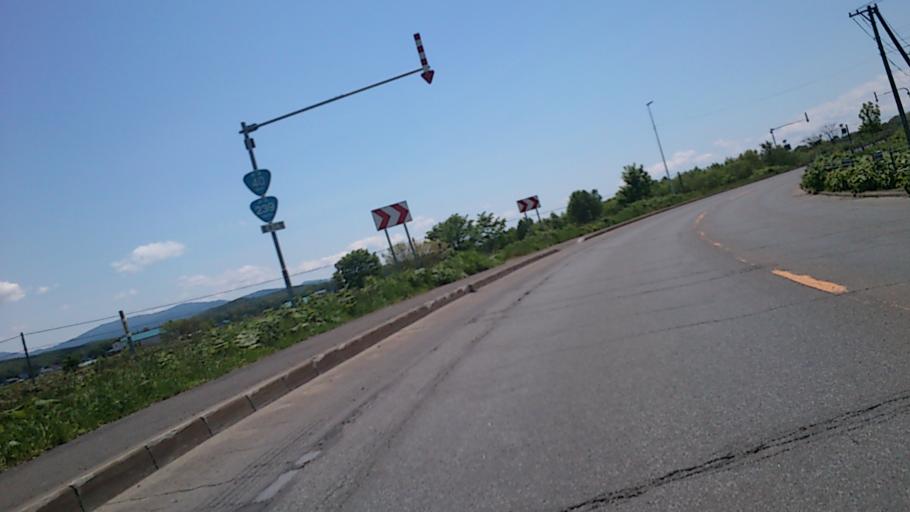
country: JP
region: Hokkaido
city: Nayoro
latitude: 44.3158
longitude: 142.4569
